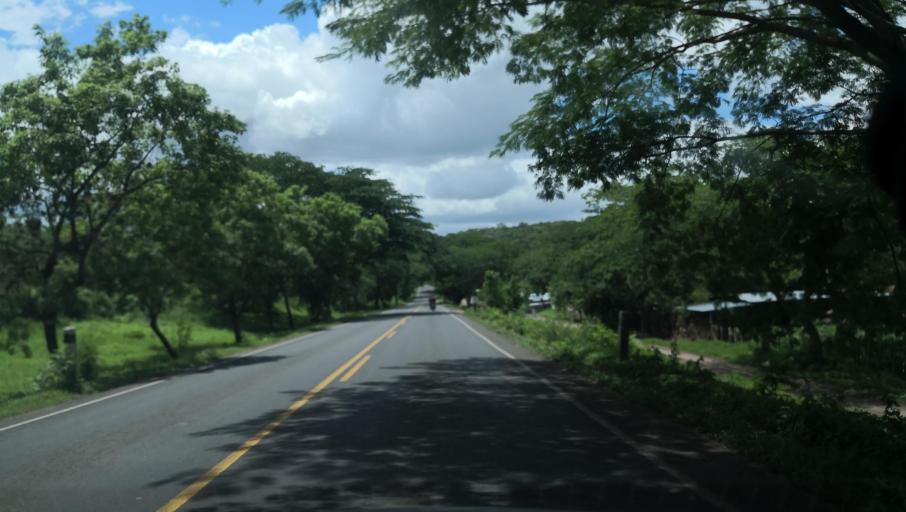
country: NI
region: Esteli
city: Condega
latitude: 13.3816
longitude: -86.4015
